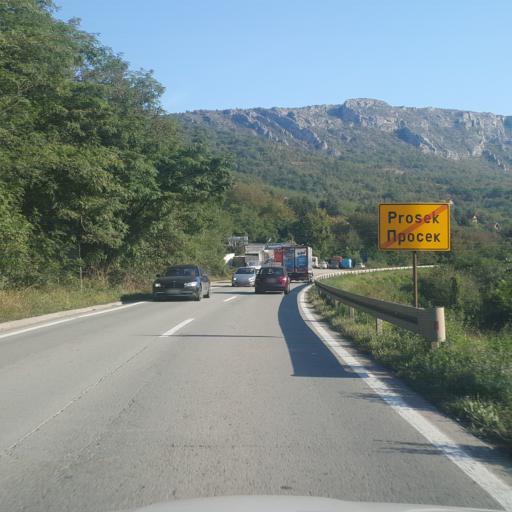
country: RS
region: Central Serbia
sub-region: Nisavski Okrug
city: Niska Banja
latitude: 43.3219
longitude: 22.0505
